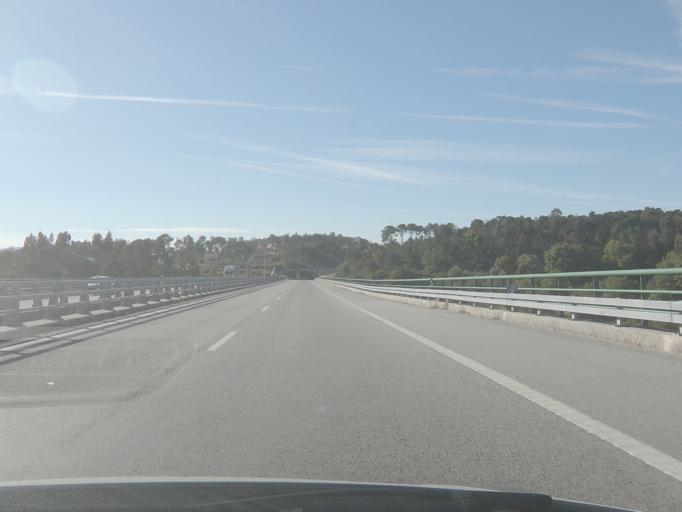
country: PT
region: Viseu
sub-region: Viseu
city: Campo
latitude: 40.7728
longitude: -7.9244
